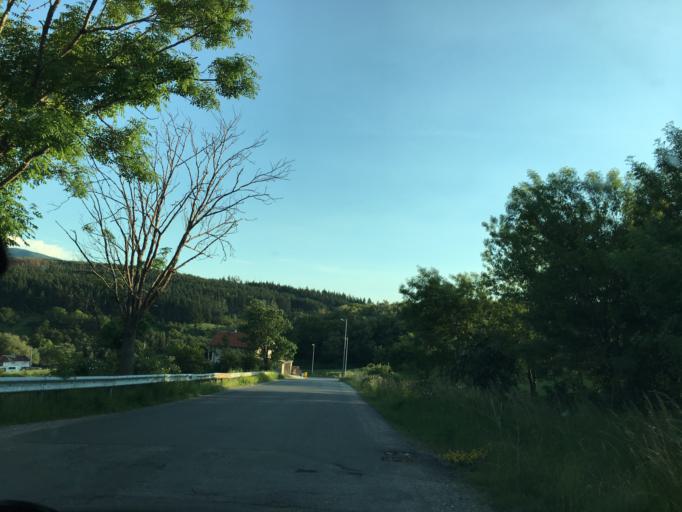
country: BG
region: Sofiya
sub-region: Obshtina Bozhurishte
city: Bozhurishte
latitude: 42.7243
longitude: 23.1278
